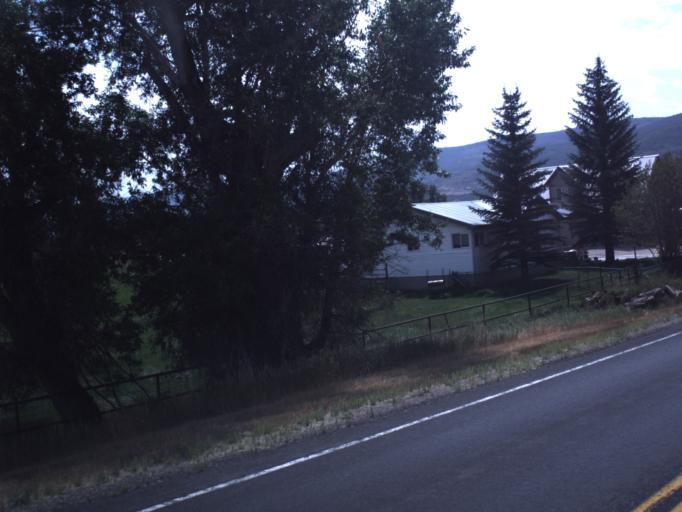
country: US
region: Utah
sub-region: Summit County
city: Francis
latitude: 40.5885
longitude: -111.2423
